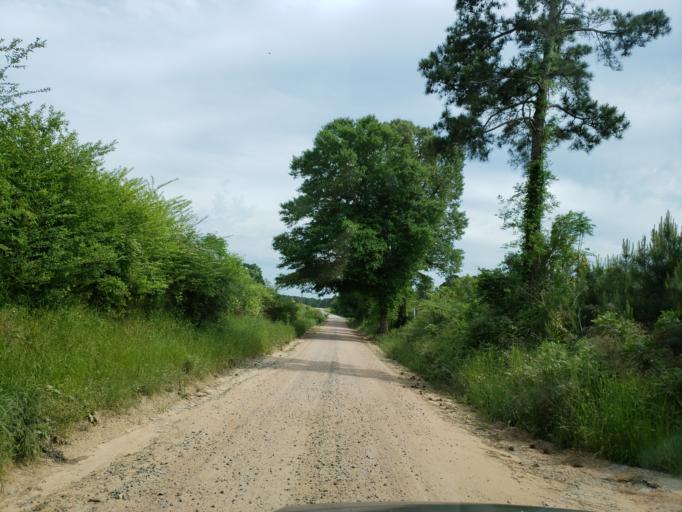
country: US
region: Georgia
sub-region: Monroe County
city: Forsyth
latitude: 32.9693
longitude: -83.9113
